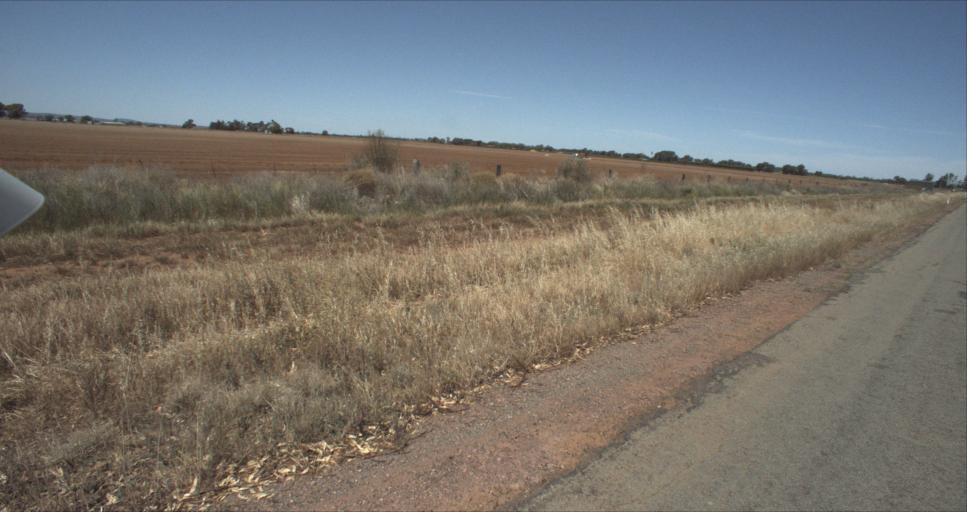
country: AU
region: New South Wales
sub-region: Leeton
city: Leeton
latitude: -34.5181
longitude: 146.3454
